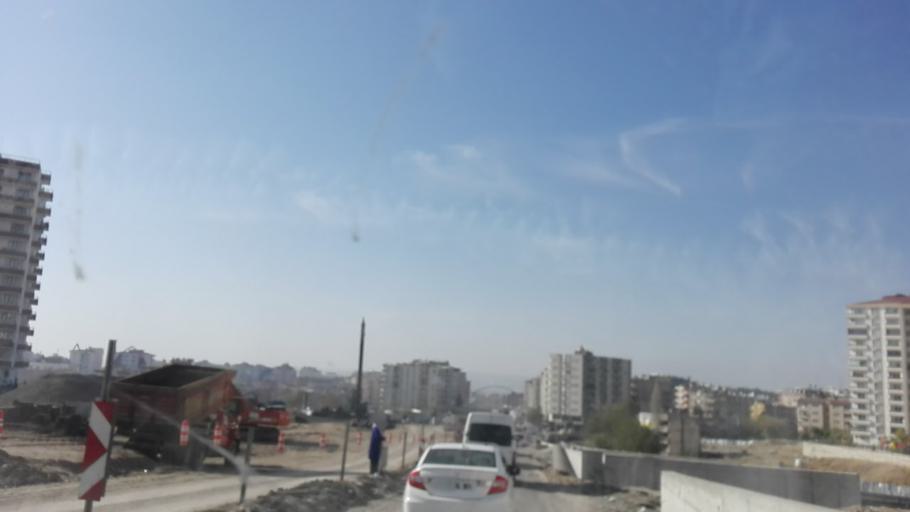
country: TR
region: Batman
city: Demiryol
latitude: 37.9030
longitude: 41.1404
